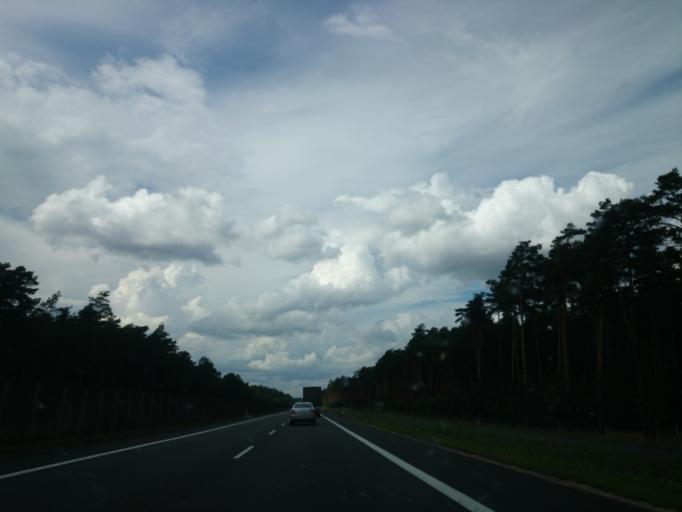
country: PL
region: Lubusz
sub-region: Powiat nowosolski
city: Otyn
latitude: 51.8815
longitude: 15.6410
